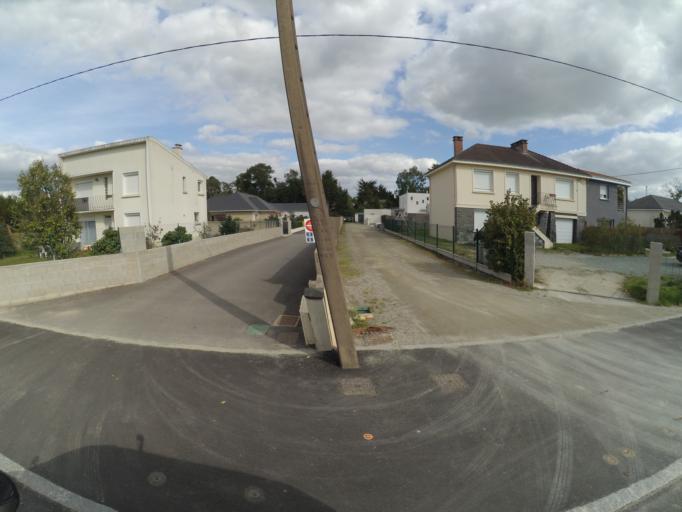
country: FR
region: Pays de la Loire
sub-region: Departement de la Loire-Atlantique
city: Carquefou
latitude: 47.3058
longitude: -1.5041
